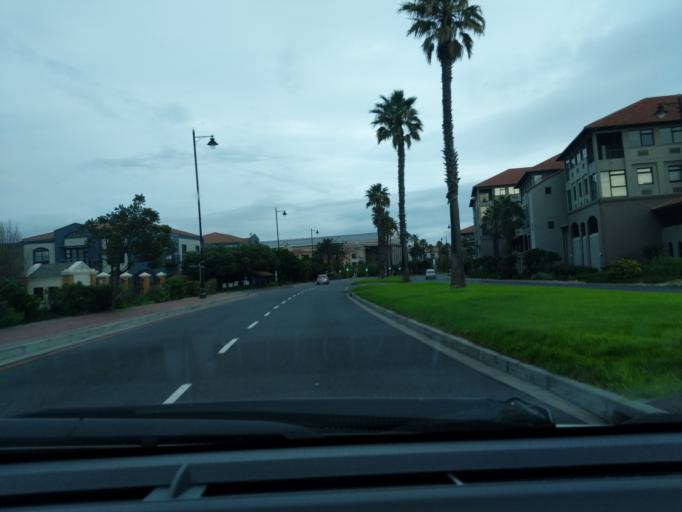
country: ZA
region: Western Cape
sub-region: City of Cape Town
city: Sunset Beach
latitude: -33.8880
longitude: 18.5200
